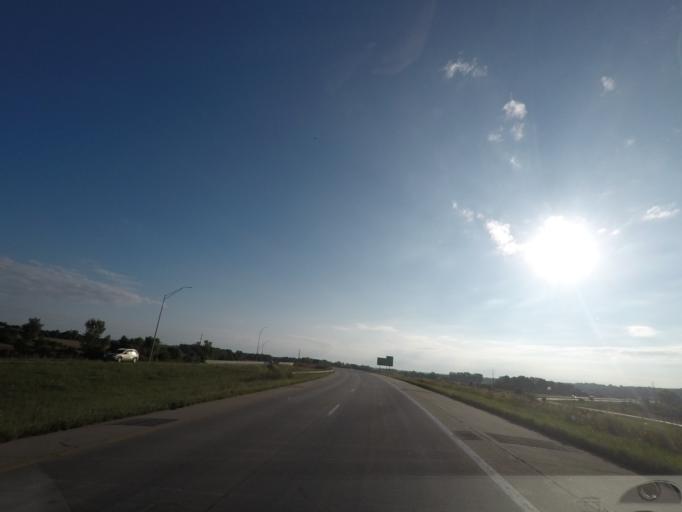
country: US
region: Iowa
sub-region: Warren County
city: Carlisle
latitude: 41.5113
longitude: -93.5264
